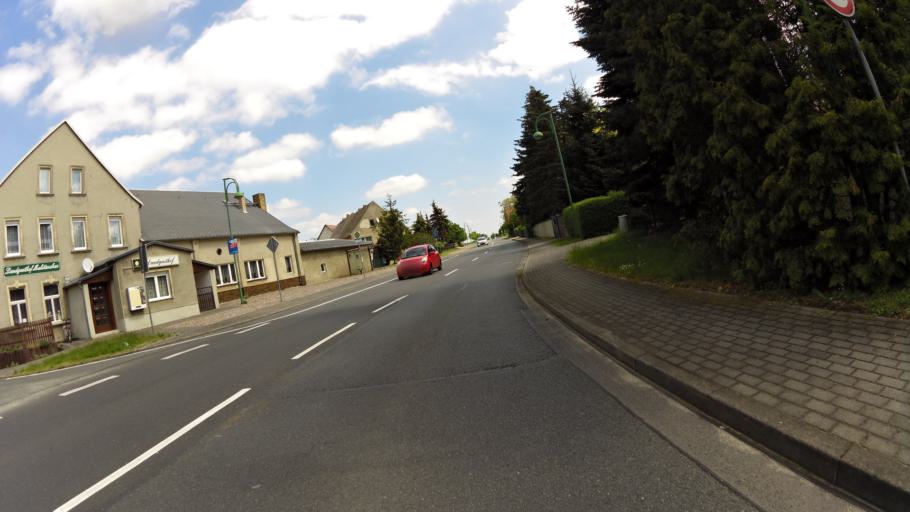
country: DE
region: Saxony
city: Belgern
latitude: 51.4872
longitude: 13.0778
